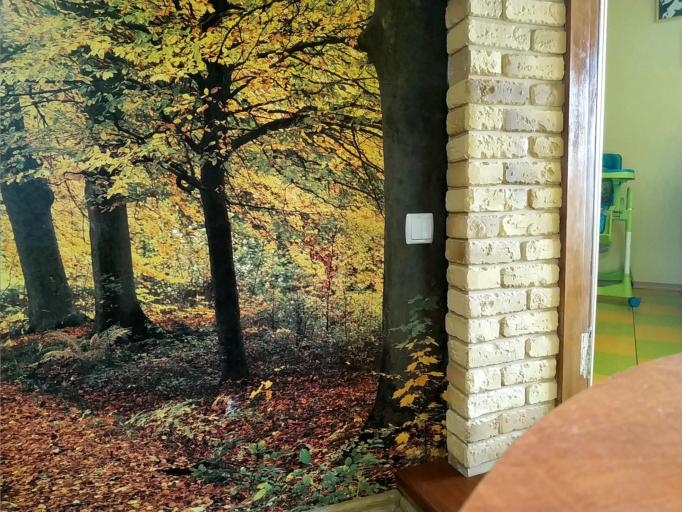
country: RU
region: Smolensk
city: Ozernyy
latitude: 55.4589
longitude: 32.6645
